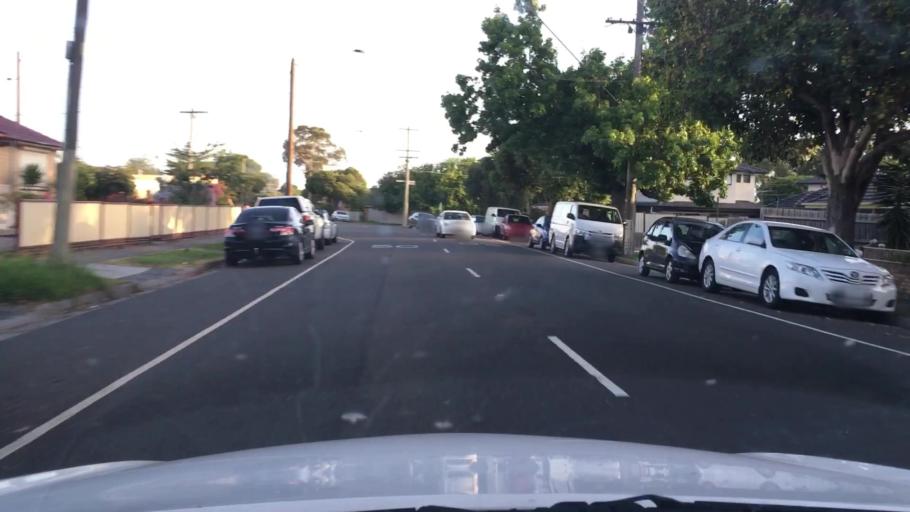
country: AU
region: Victoria
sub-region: Greater Dandenong
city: Noble Park
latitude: -37.9586
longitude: 145.1731
